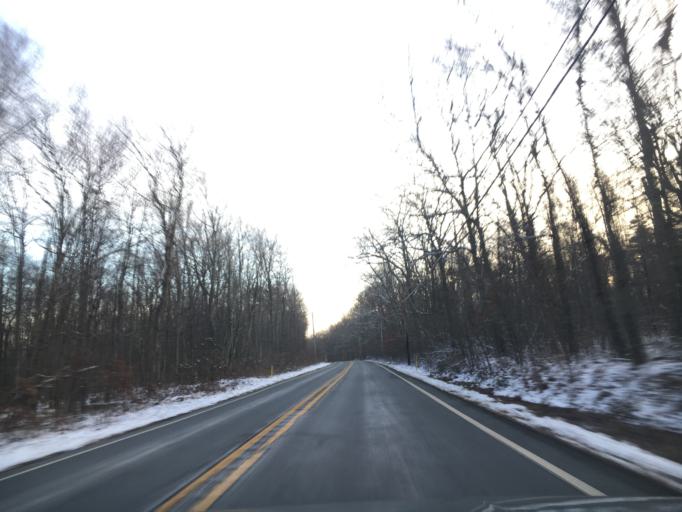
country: US
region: Pennsylvania
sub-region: Pike County
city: Saw Creek
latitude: 41.1749
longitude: -75.0827
